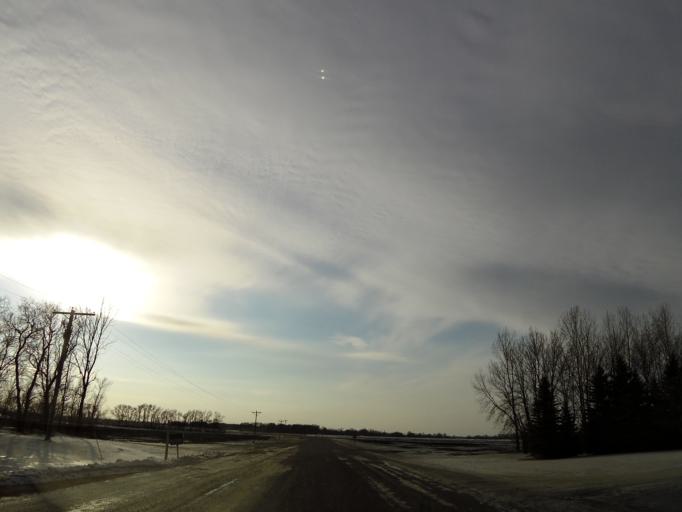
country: US
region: North Dakota
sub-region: Walsh County
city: Grafton
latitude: 48.4269
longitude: -97.3490
